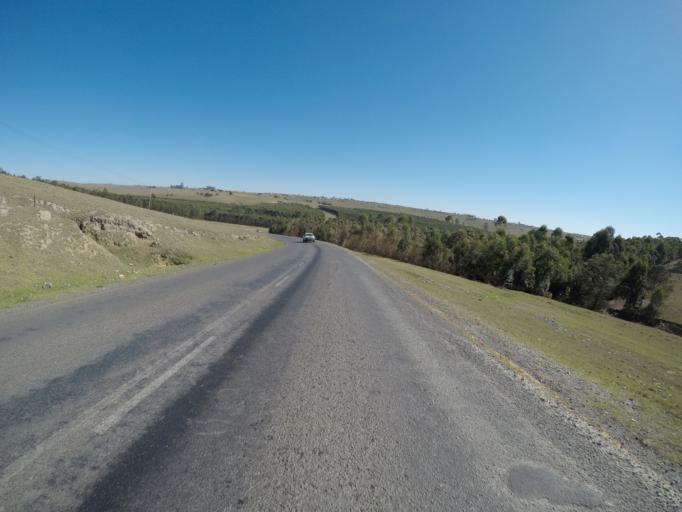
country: ZA
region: Eastern Cape
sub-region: OR Tambo District Municipality
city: Mthatha
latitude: -31.7798
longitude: 28.7380
